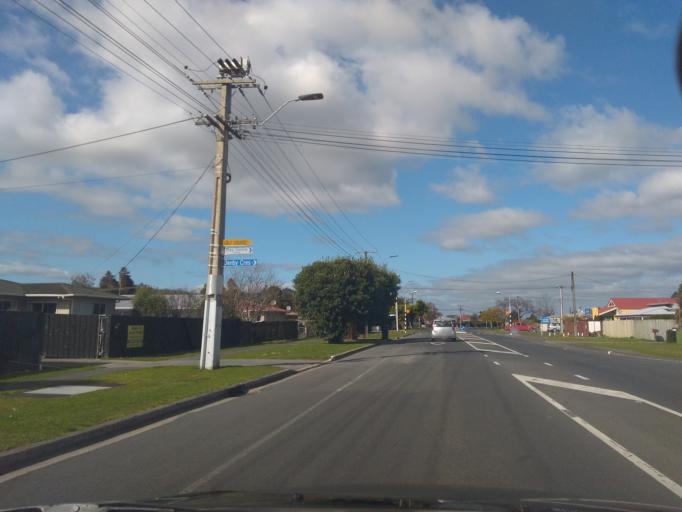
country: NZ
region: Northland
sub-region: Whangarei
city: Whangarei
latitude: -35.6902
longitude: 174.3271
